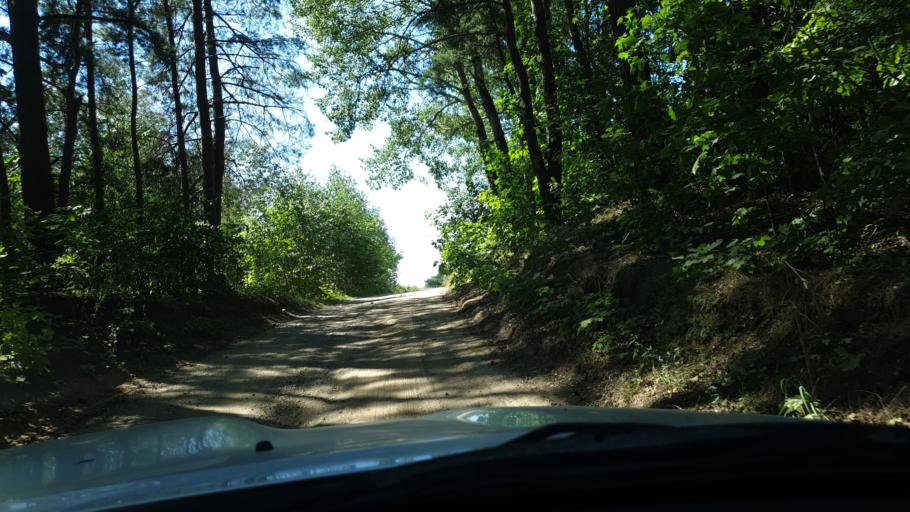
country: LT
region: Vilnius County
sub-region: Vilniaus Rajonas
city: Vievis
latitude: 54.8990
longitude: 24.8741
